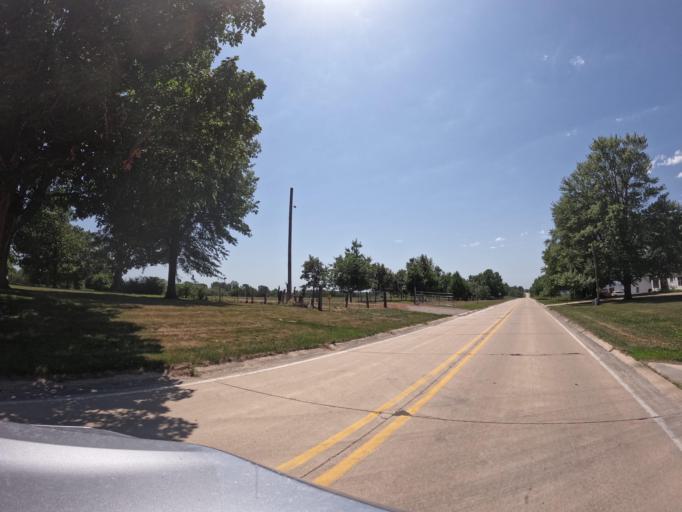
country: US
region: Iowa
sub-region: Henry County
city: Mount Pleasant
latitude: 40.9538
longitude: -91.5544
